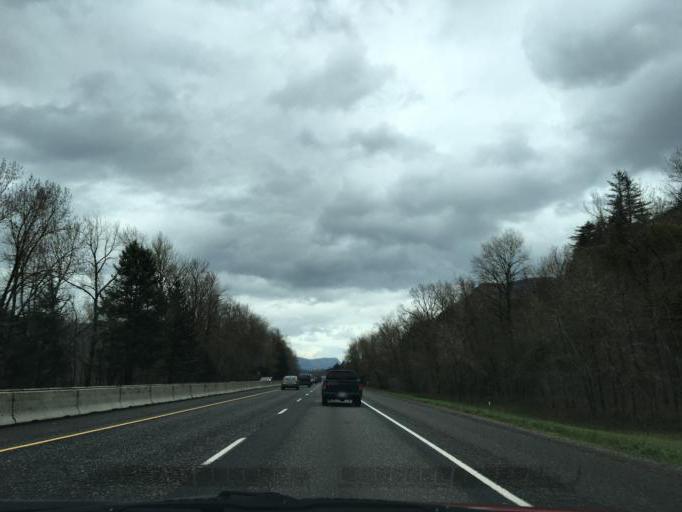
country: US
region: Washington
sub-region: Clark County
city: Washougal
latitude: 45.5543
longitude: -122.1864
